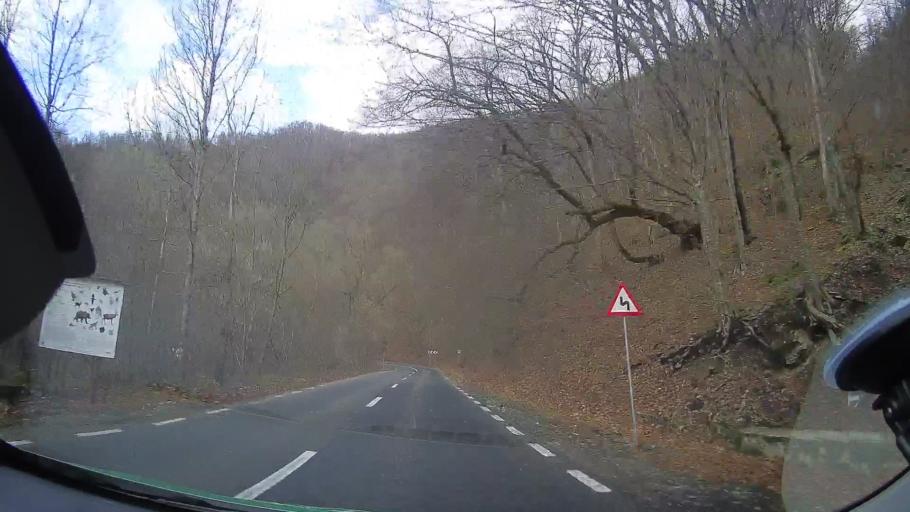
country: RO
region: Cluj
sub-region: Comuna Valea Ierii
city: Valea Ierii
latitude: 46.6299
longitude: 23.3837
